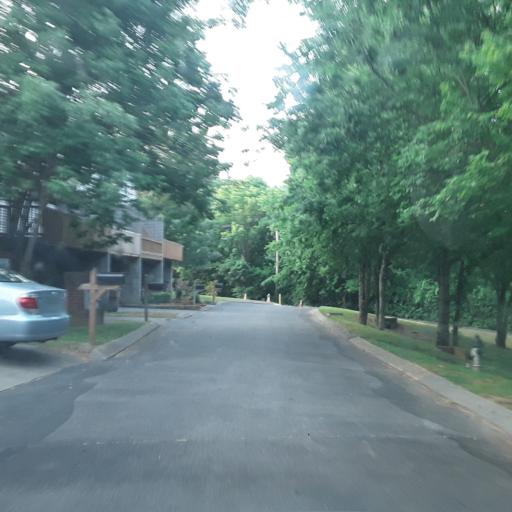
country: US
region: Tennessee
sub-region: Williamson County
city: Brentwood
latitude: 36.0520
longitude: -86.7308
